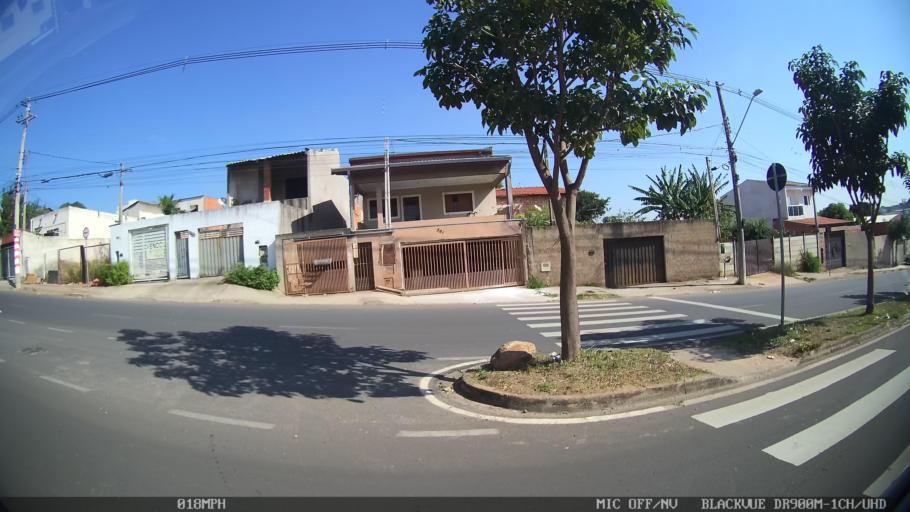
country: BR
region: Sao Paulo
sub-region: Campinas
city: Campinas
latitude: -22.9485
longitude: -47.0794
